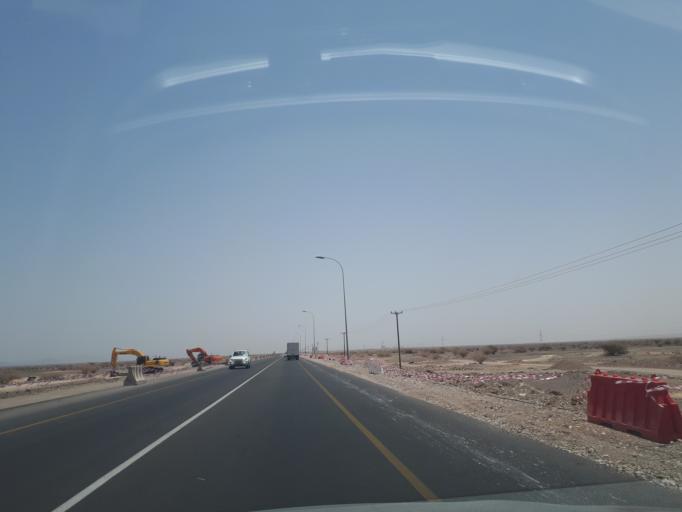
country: OM
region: Ash Sharqiyah
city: Badiyah
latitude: 22.4271
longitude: 59.0384
